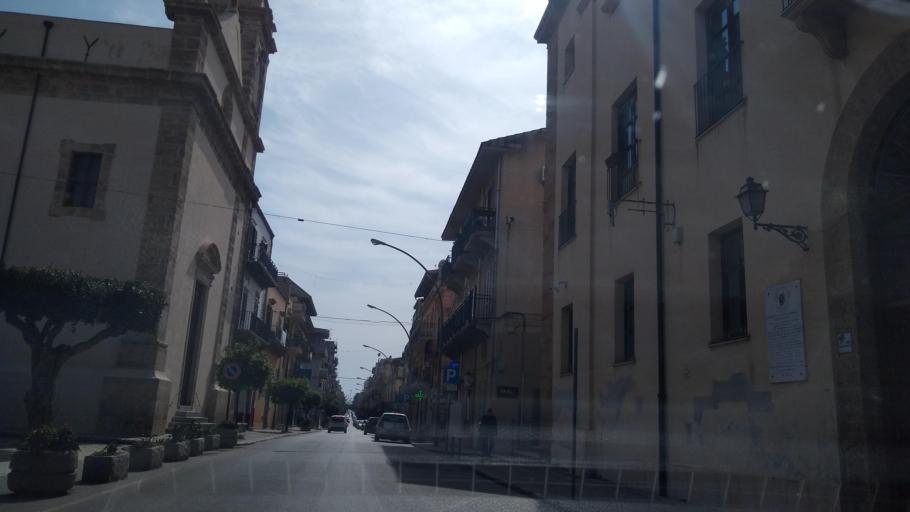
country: IT
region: Sicily
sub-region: Palermo
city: Partinico
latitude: 38.0455
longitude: 13.1166
